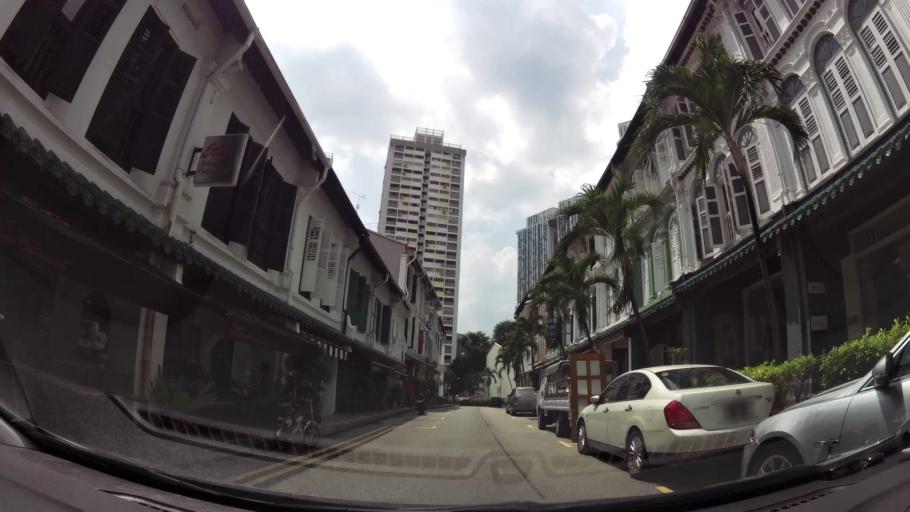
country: SG
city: Singapore
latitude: 1.2784
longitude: 103.8432
